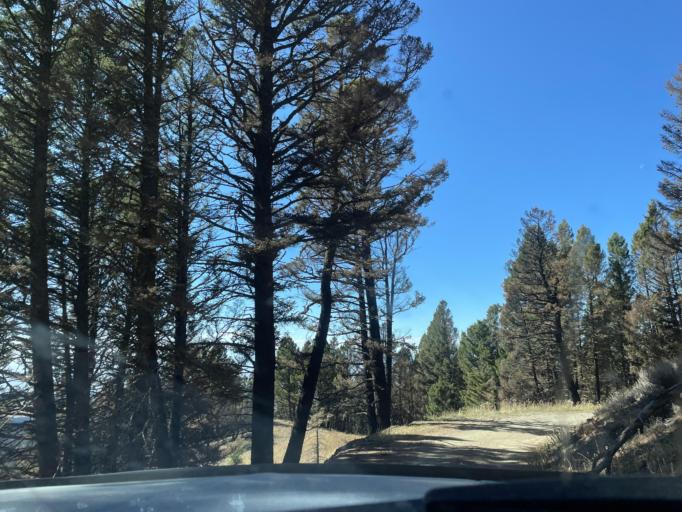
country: US
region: Montana
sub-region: Broadwater County
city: Townsend
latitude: 46.5065
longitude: -111.2829
